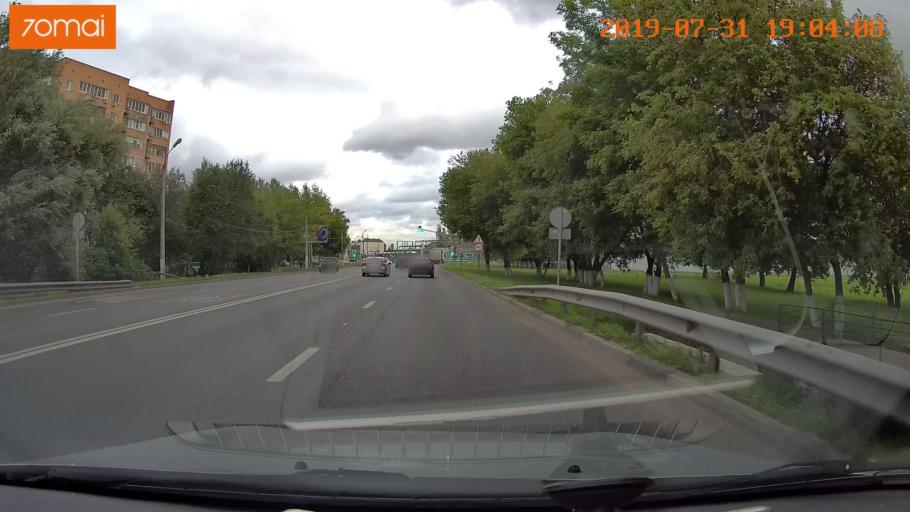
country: RU
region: Moskovskaya
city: Raduzhnyy
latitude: 55.1107
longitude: 38.7394
